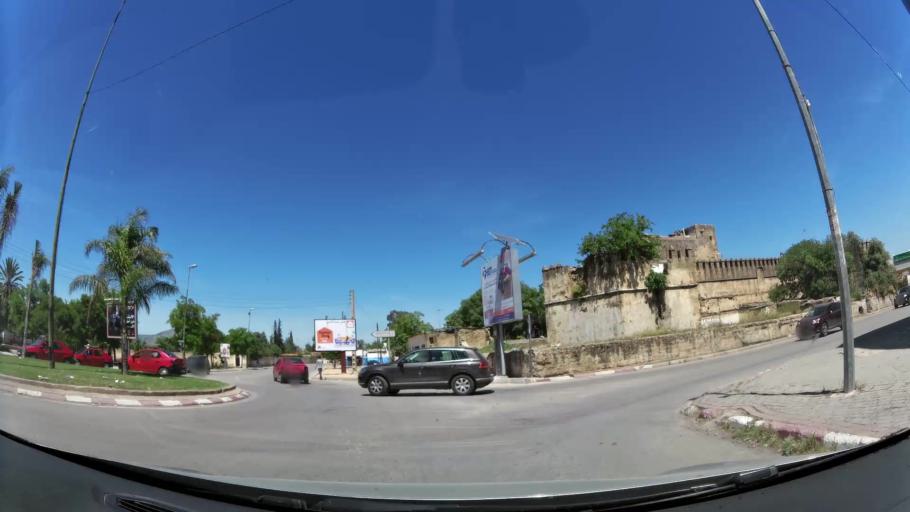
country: MA
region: Fes-Boulemane
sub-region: Fes
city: Fes
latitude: 34.0278
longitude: -5.0025
